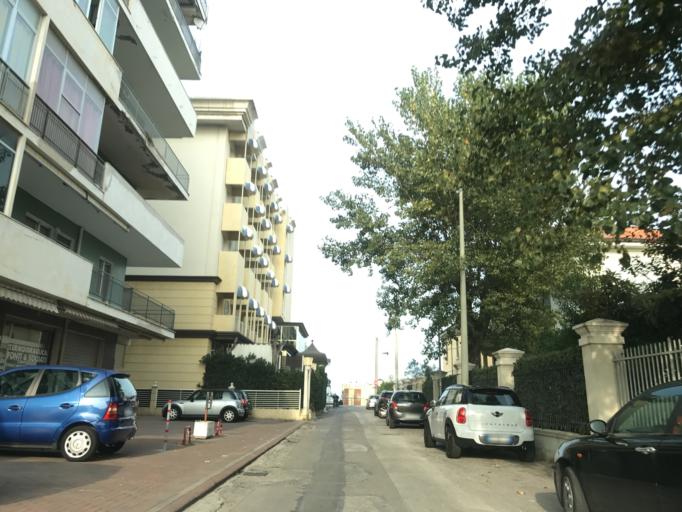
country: IT
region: Emilia-Romagna
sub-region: Provincia di Rimini
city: Rimini
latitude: 44.0833
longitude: 12.5439
